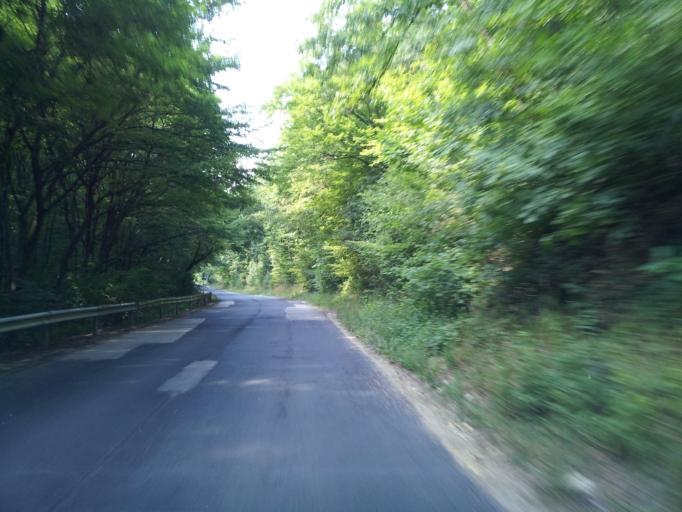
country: HU
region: Veszprem
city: Balatonfured
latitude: 46.9872
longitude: 17.8164
